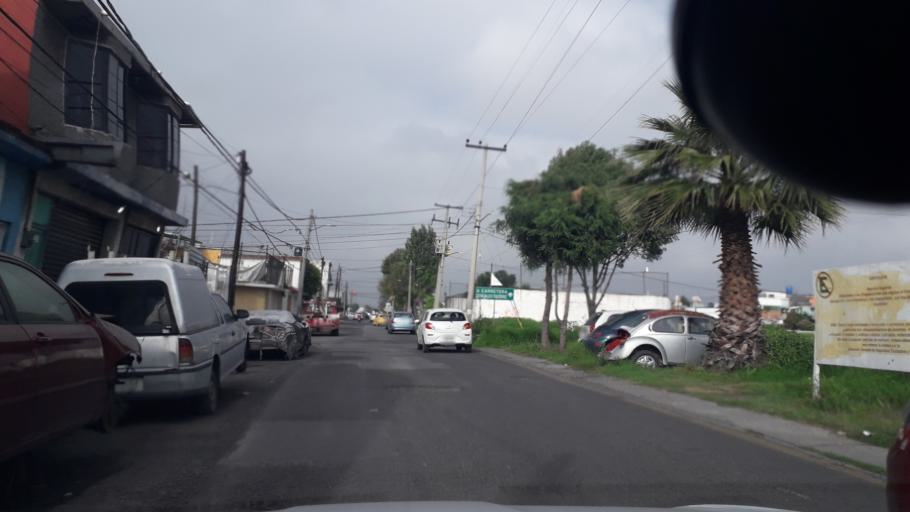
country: MX
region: Mexico
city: Coacalco
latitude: 19.6449
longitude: -99.1003
